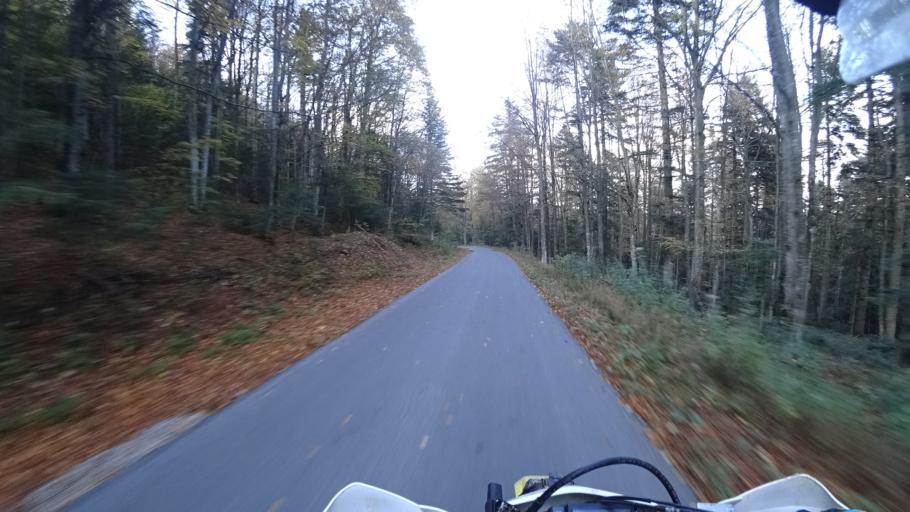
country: HR
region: Karlovacka
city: Plaski
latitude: 44.9698
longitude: 15.3874
